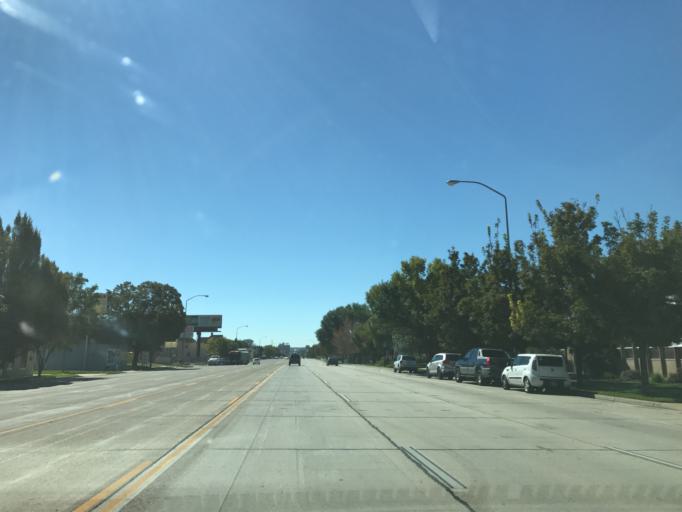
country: US
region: Utah
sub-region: Weber County
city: Ogden
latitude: 41.2425
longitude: -111.9700
